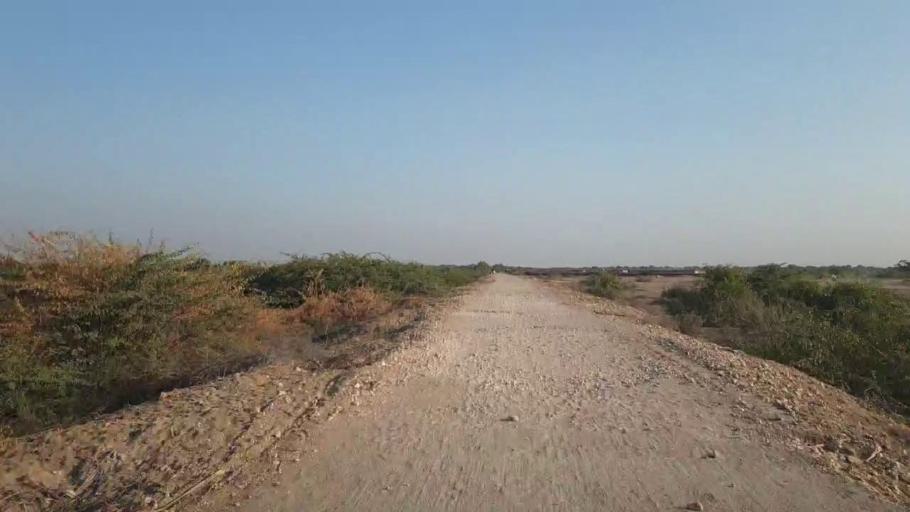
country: PK
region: Sindh
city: Mirpur Khas
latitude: 25.4258
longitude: 68.9024
